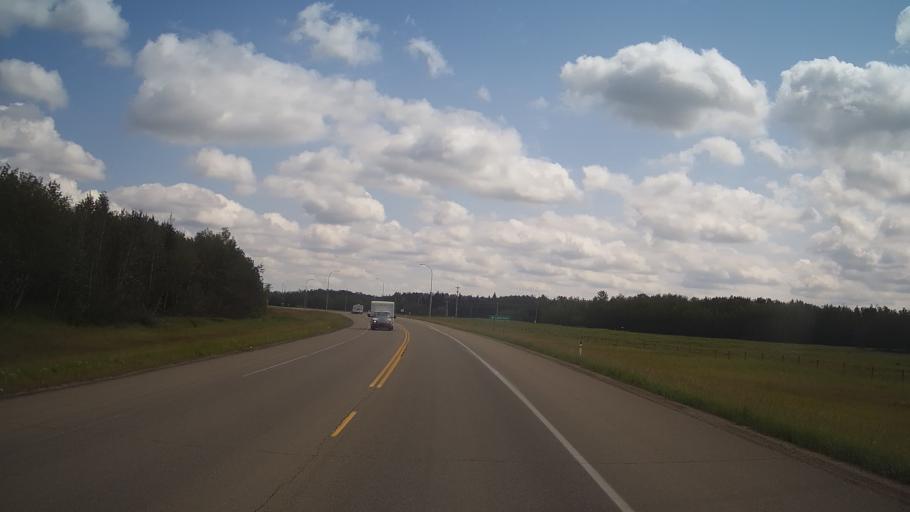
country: CA
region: Alberta
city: Sherwood Park
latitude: 53.3972
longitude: -113.1032
